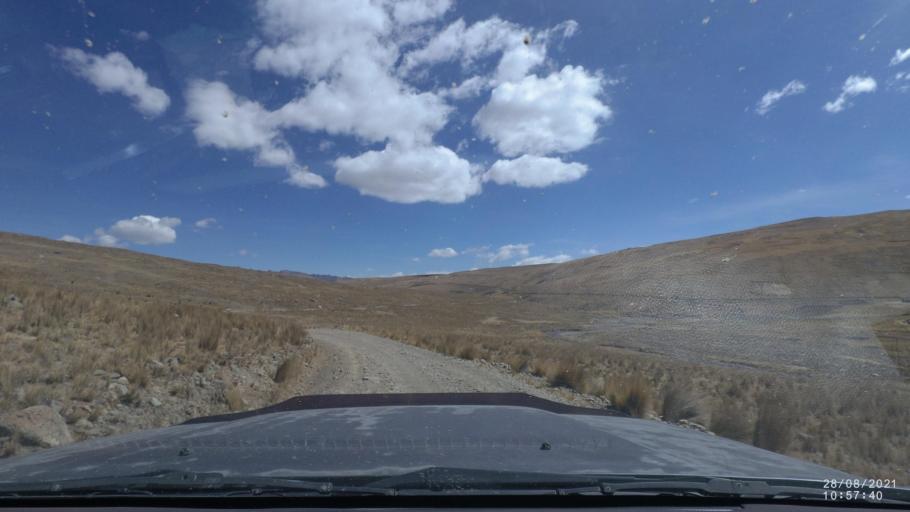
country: BO
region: Cochabamba
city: Cochabamba
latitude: -17.1882
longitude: -66.2515
